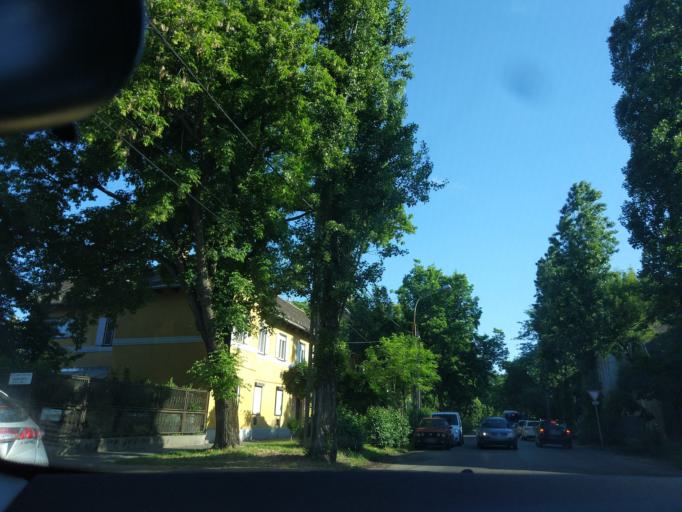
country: HU
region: Budapest
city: Budapest XIX. keruelet
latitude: 47.4537
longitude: 19.1258
